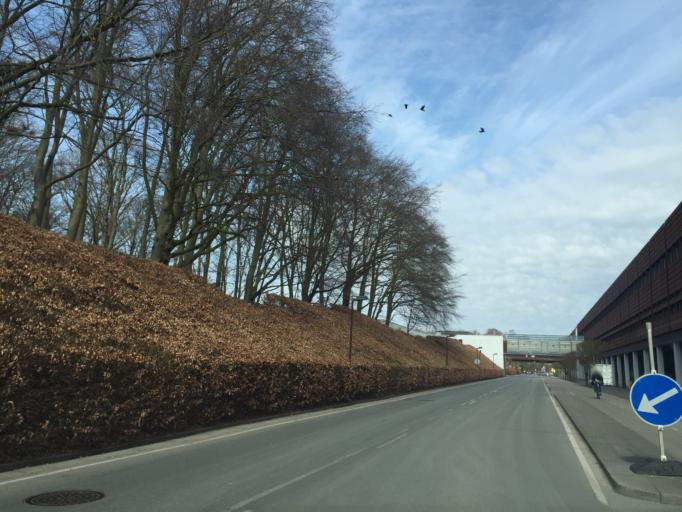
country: DK
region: South Denmark
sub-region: Odense Kommune
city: Neder Holluf
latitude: 55.3684
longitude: 10.4280
